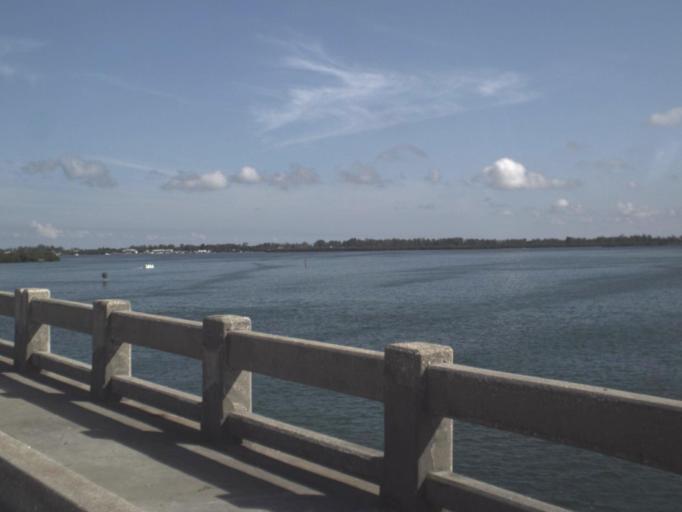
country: US
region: Florida
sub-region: Manatee County
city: Cortez
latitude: 27.4435
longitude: -82.6876
